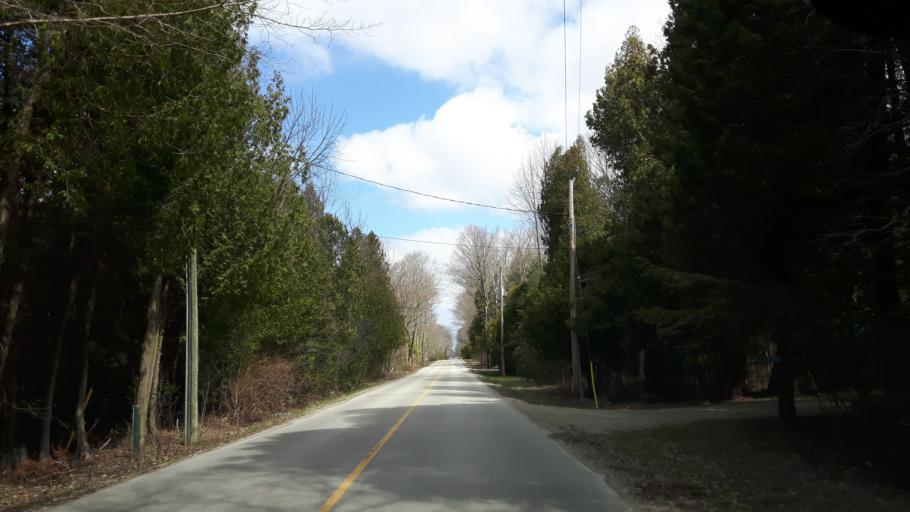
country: CA
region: Ontario
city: Bluewater
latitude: 43.5808
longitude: -81.6848
